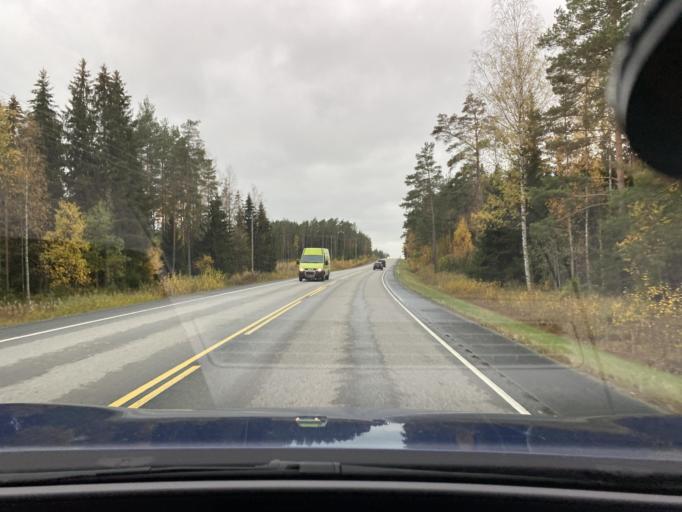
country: FI
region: Satakunta
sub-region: Rauma
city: Lappi
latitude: 61.1092
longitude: 21.9192
